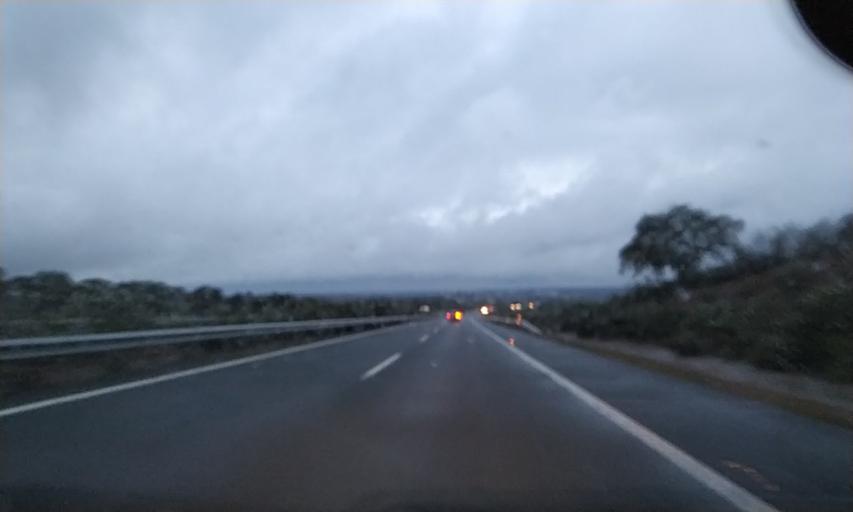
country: ES
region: Extremadura
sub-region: Provincia de Caceres
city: Alcuescar
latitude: 39.1790
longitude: -6.2733
